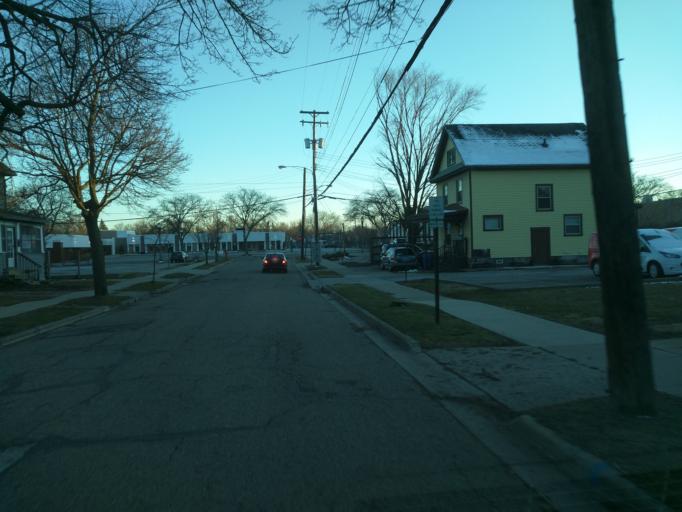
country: US
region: Michigan
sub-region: Ingham County
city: Lansing
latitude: 42.7344
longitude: -84.5313
